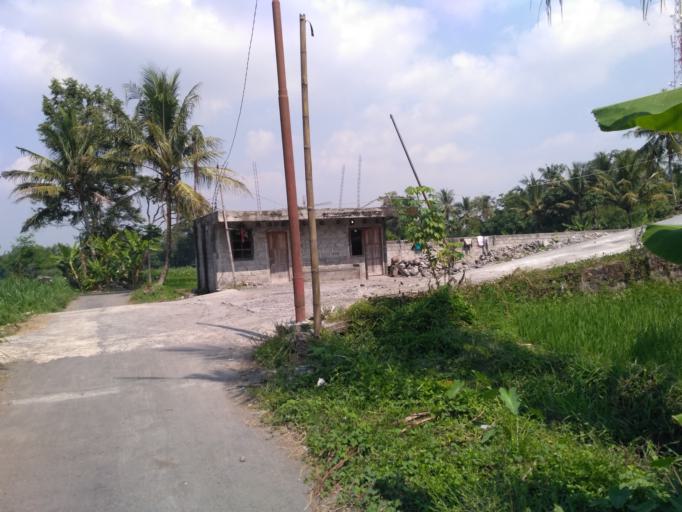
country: ID
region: Daerah Istimewa Yogyakarta
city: Melati
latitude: -7.7075
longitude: 110.4138
